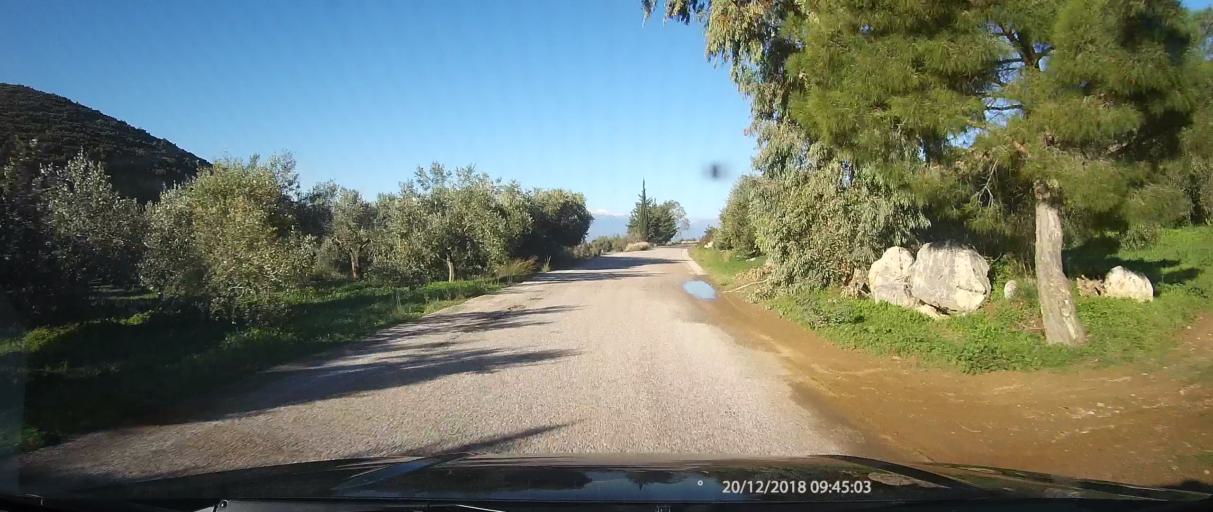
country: GR
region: Peloponnese
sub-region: Nomos Lakonias
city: Yerakion
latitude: 36.9817
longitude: 22.7325
